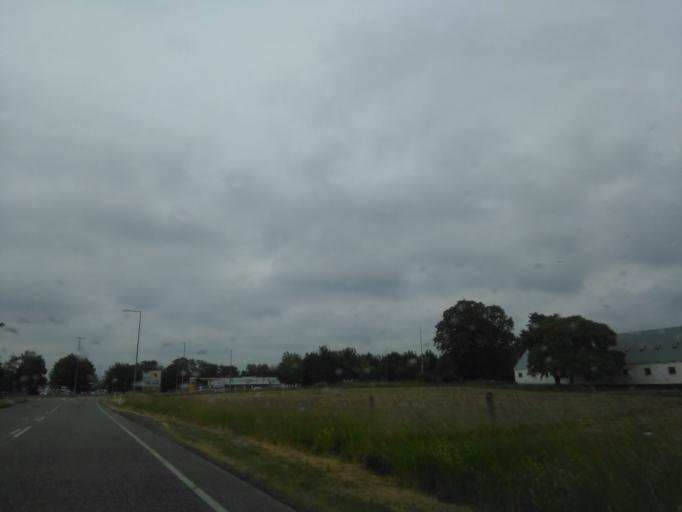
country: DK
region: Capital Region
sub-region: Bornholm Kommune
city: Ronne
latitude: 55.0917
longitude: 14.7281
